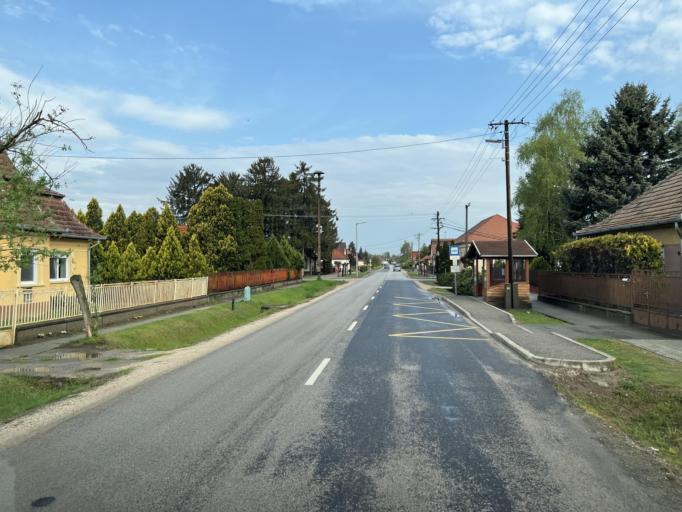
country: HU
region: Pest
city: Nyaregyhaza
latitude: 47.2274
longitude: 19.4532
